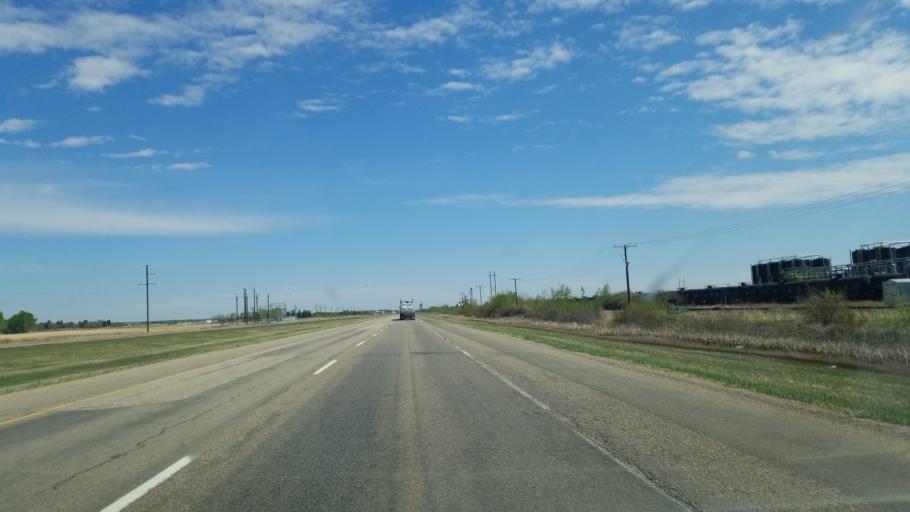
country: CA
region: Saskatchewan
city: Lloydminster
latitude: 53.1406
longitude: -109.6568
